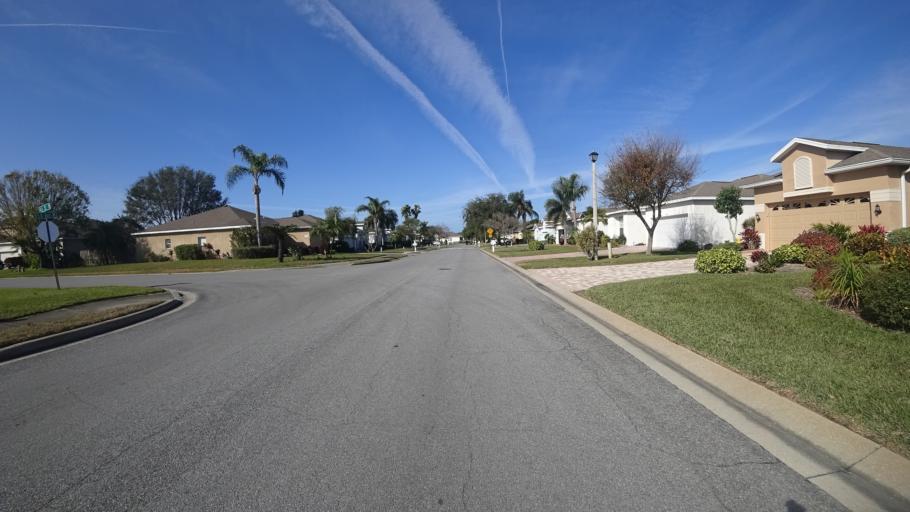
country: US
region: Florida
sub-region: Manatee County
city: South Bradenton
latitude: 27.4548
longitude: -82.6063
